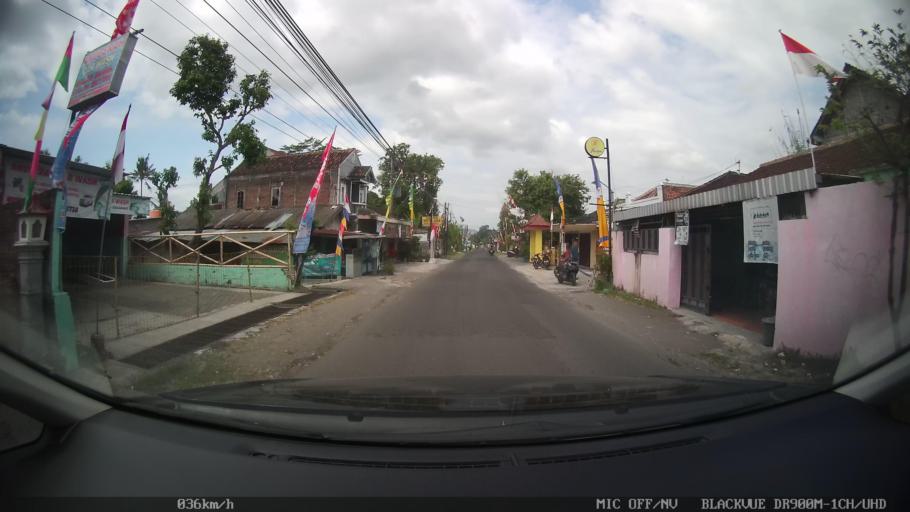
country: ID
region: Daerah Istimewa Yogyakarta
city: Depok
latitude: -7.7839
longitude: 110.4639
